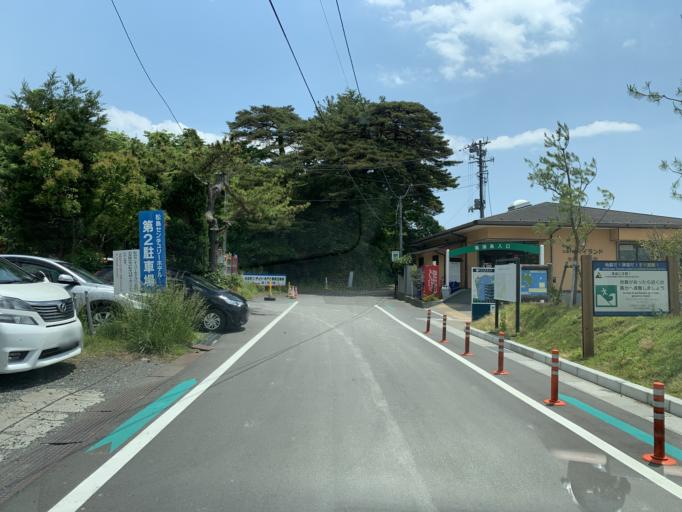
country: JP
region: Miyagi
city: Matsushima
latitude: 38.3703
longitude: 141.0677
